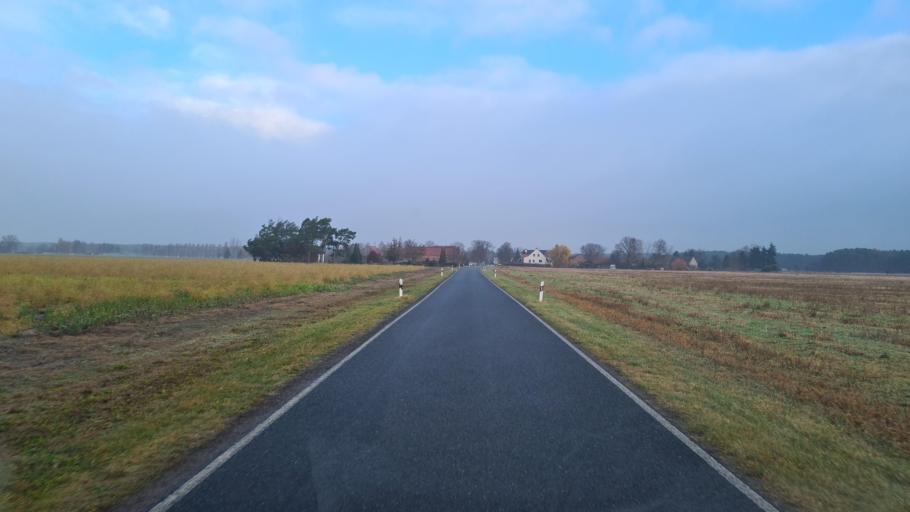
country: DE
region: Brandenburg
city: Beelitz
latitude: 52.1517
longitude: 12.9678
